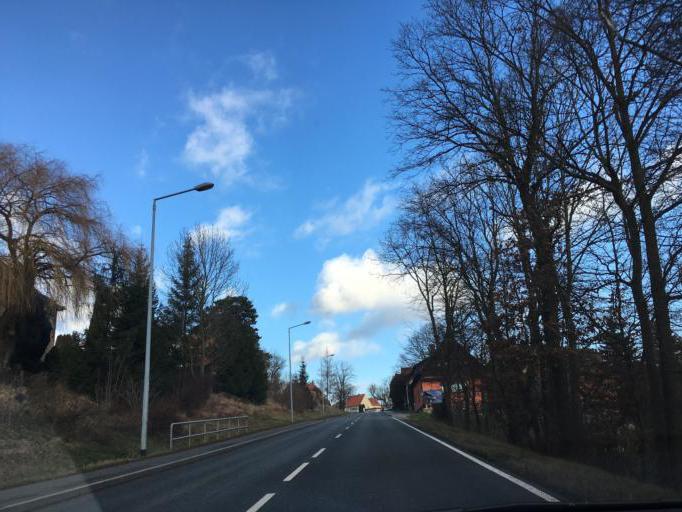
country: DE
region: Thuringia
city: Hetschburg
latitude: 50.9309
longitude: 11.2922
